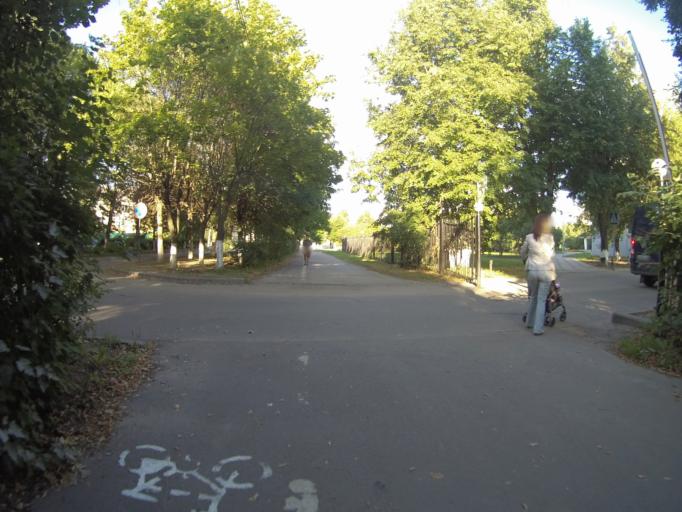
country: RU
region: Vladimir
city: Vladimir
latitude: 56.1471
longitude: 40.3777
